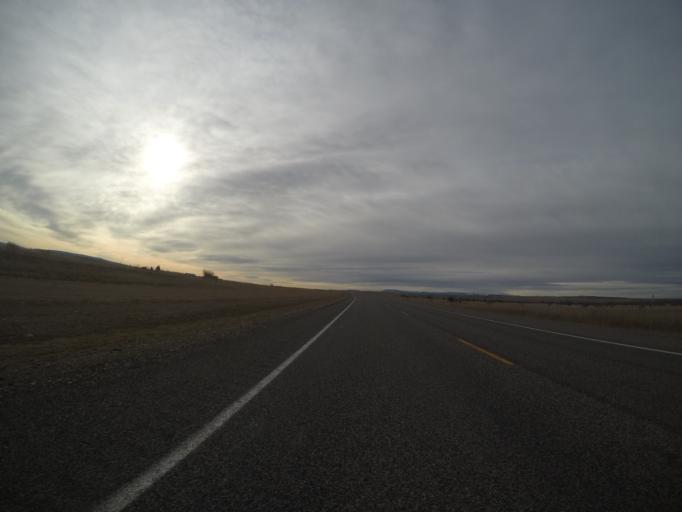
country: US
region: Montana
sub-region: Yellowstone County
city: Laurel
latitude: 45.5842
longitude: -108.8401
